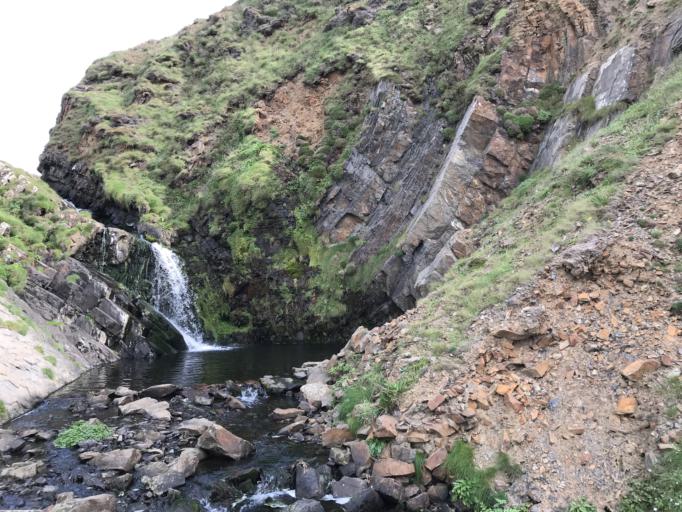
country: GB
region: England
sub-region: Cornwall
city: Flexbury
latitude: 51.0120
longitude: -4.5257
